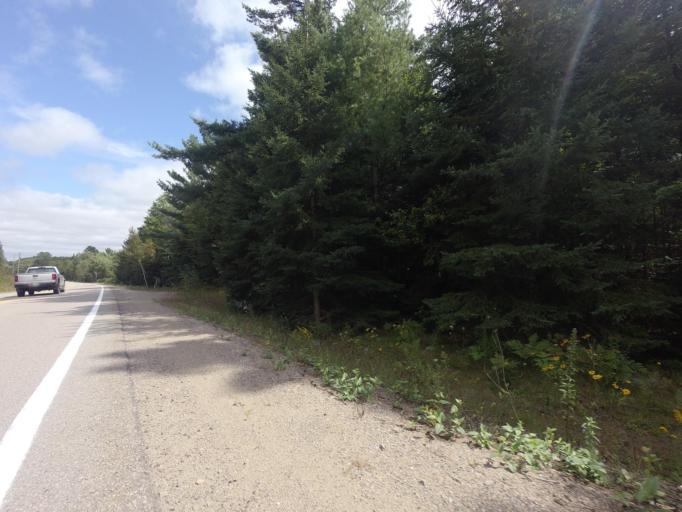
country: CA
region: Ontario
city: Omemee
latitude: 44.8781
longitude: -78.5100
